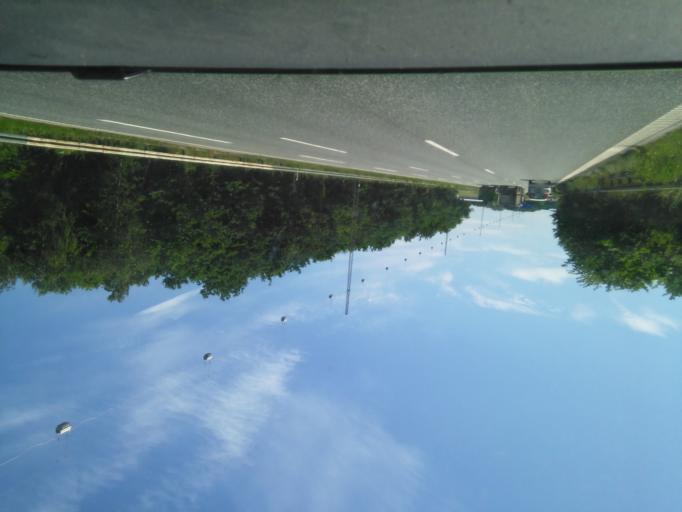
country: DK
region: Capital Region
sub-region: Hoje-Taastrup Kommune
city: Taastrup
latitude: 55.6650
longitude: 12.2946
